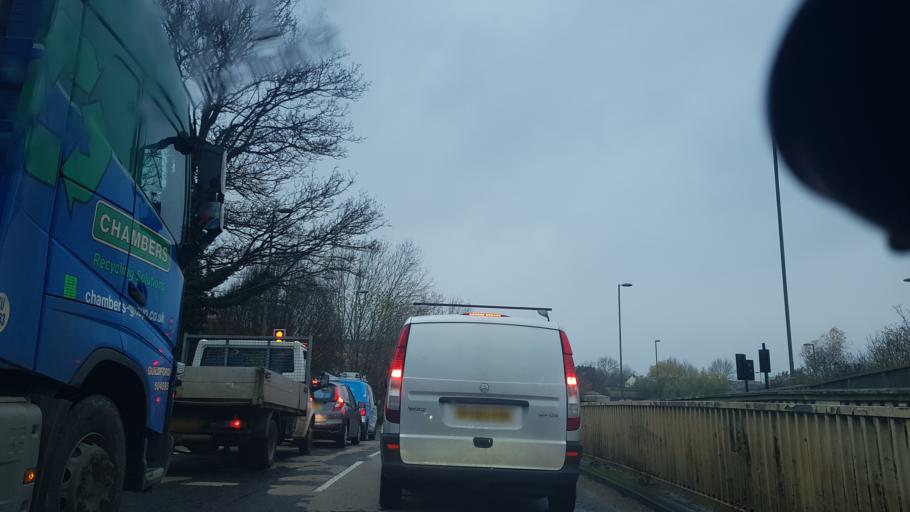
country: GB
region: England
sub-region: Surrey
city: Guildford
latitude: 51.2475
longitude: -0.5814
